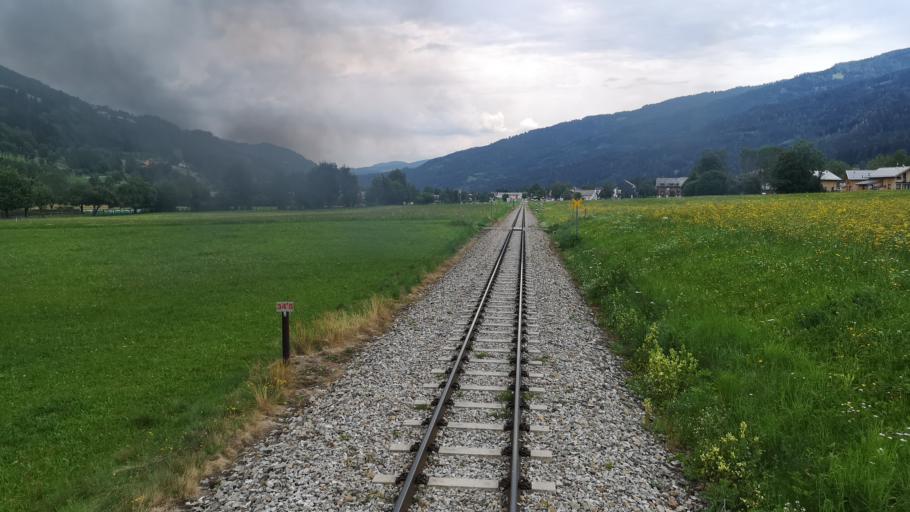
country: AT
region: Styria
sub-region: Politischer Bezirk Murau
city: Sankt Georgen ob Murau
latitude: 47.1025
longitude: 14.0809
